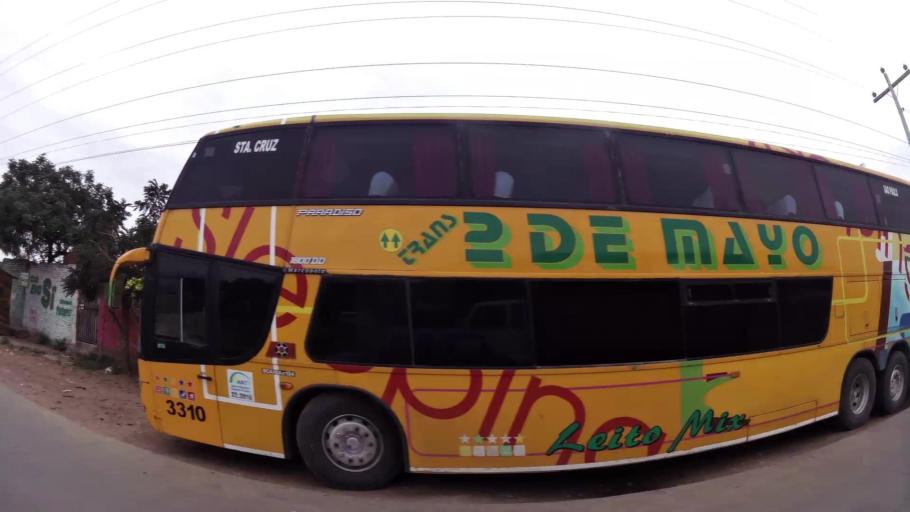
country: BO
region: Santa Cruz
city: Santa Cruz de la Sierra
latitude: -17.8229
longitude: -63.1800
